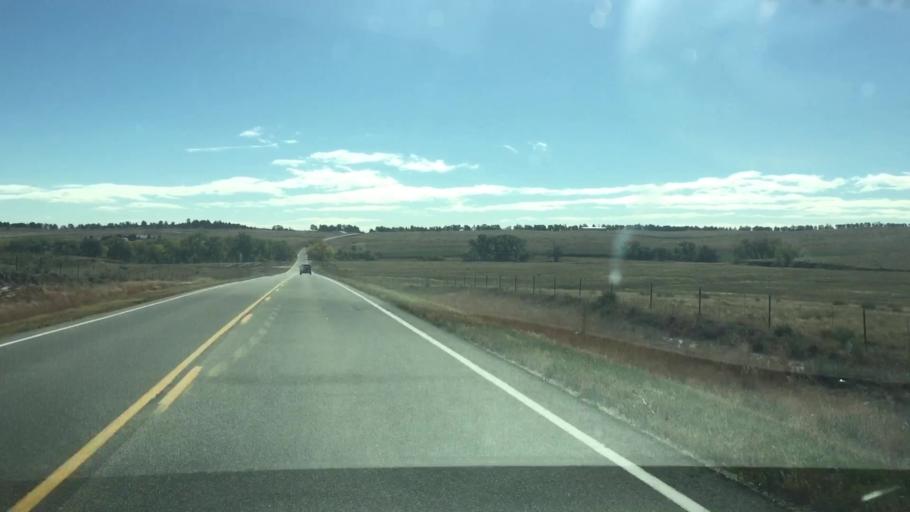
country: US
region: Colorado
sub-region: Elbert County
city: Kiowa
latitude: 39.3230
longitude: -104.3883
